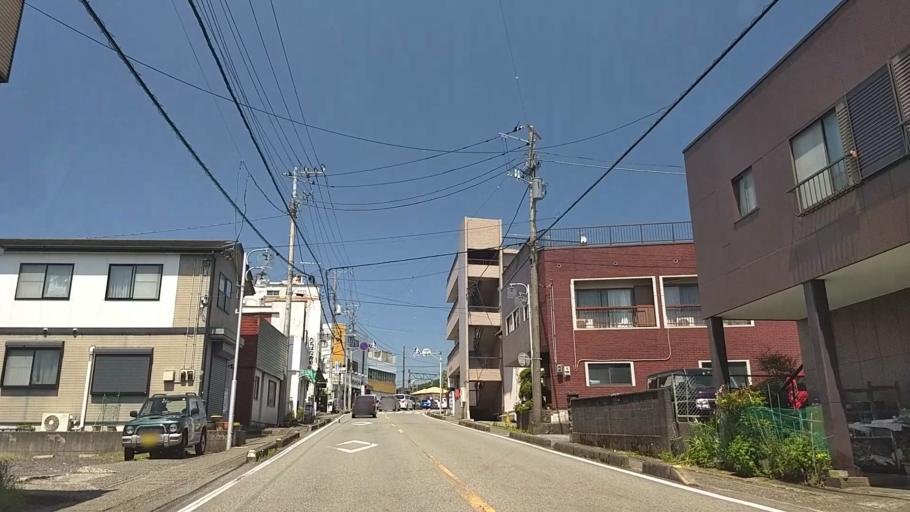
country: JP
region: Shizuoka
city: Gotemba
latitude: 35.2152
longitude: 138.9184
